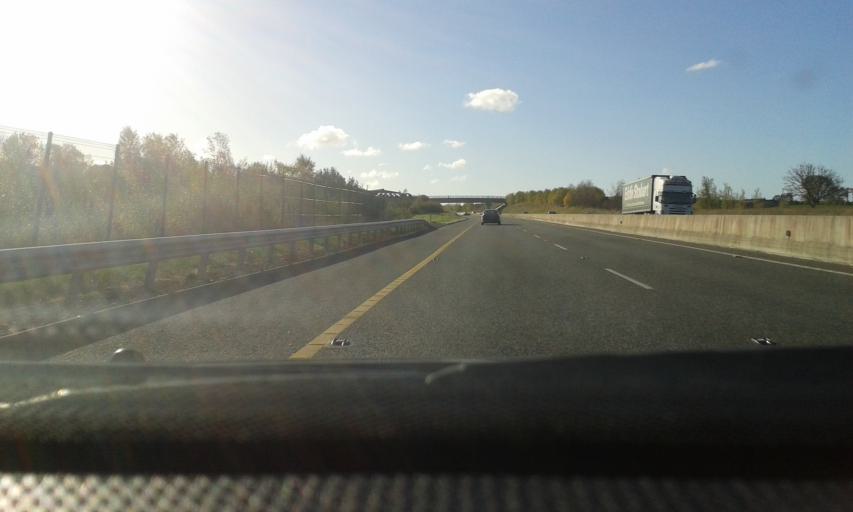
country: IE
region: Leinster
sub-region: Laois
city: Rathdowney
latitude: 52.8441
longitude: -7.4978
